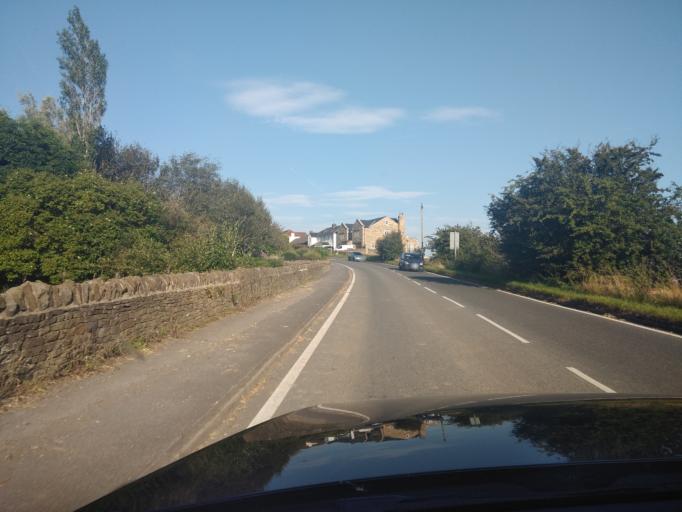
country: GB
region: England
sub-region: Derbyshire
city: Dronfield
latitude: 53.2944
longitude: -1.5248
